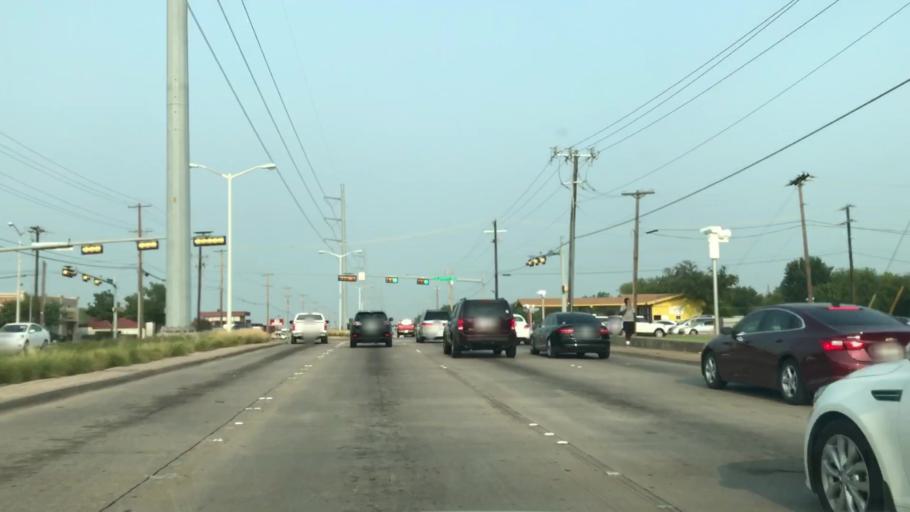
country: US
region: Texas
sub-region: Dallas County
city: Garland
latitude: 32.9092
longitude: -96.6837
